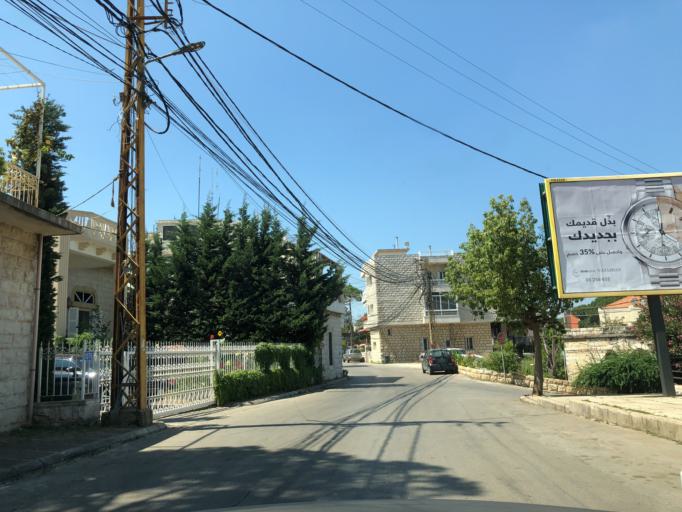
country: LB
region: Mont-Liban
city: Jdaidet el Matn
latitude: 33.8673
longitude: 35.6051
